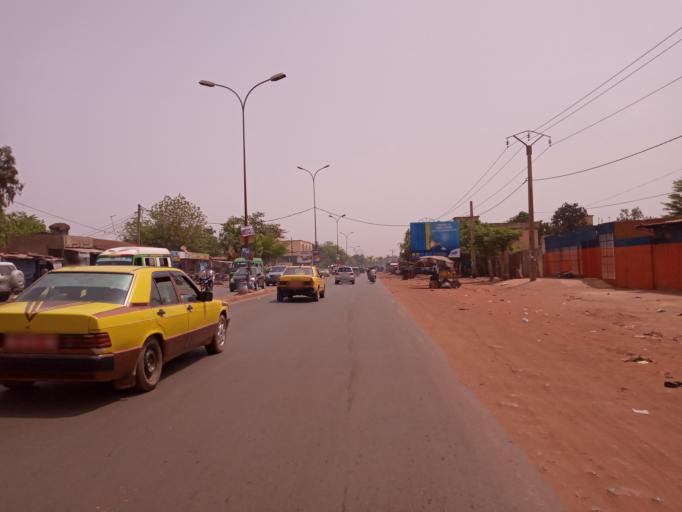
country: ML
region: Bamako
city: Bamako
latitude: 12.6621
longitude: -7.9538
